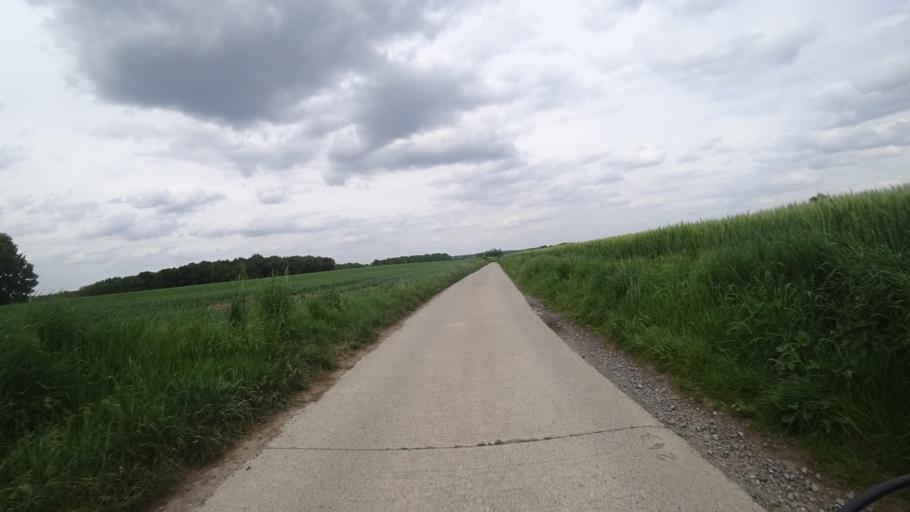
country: BE
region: Wallonia
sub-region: Province du Brabant Wallon
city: Grez-Doiceau
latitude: 50.7060
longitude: 4.6783
